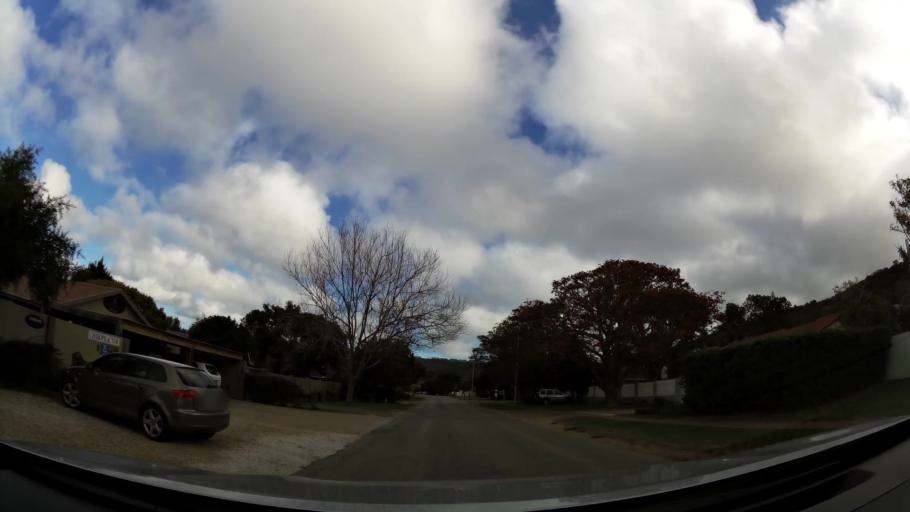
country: ZA
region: Western Cape
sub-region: Eden District Municipality
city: Plettenberg Bay
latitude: -34.0785
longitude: 23.3643
